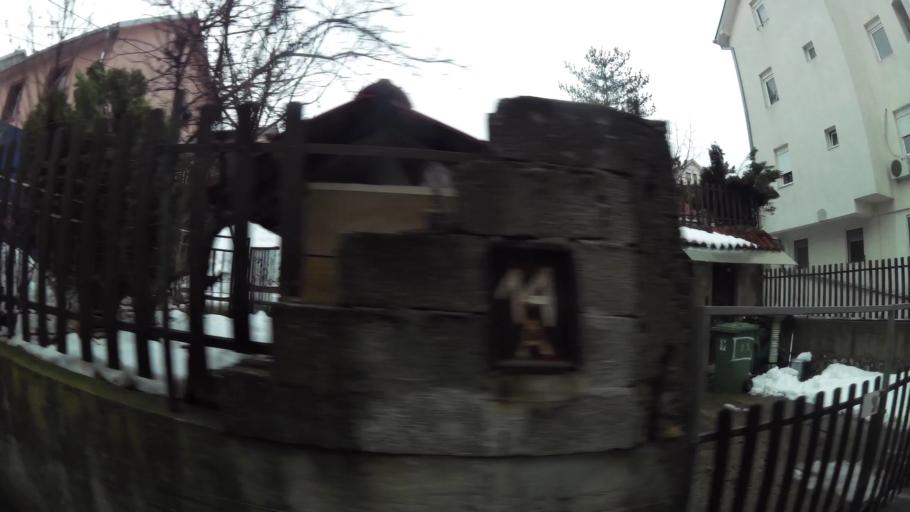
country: RS
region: Central Serbia
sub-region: Belgrade
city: Zvezdara
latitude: 44.7705
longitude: 20.5087
